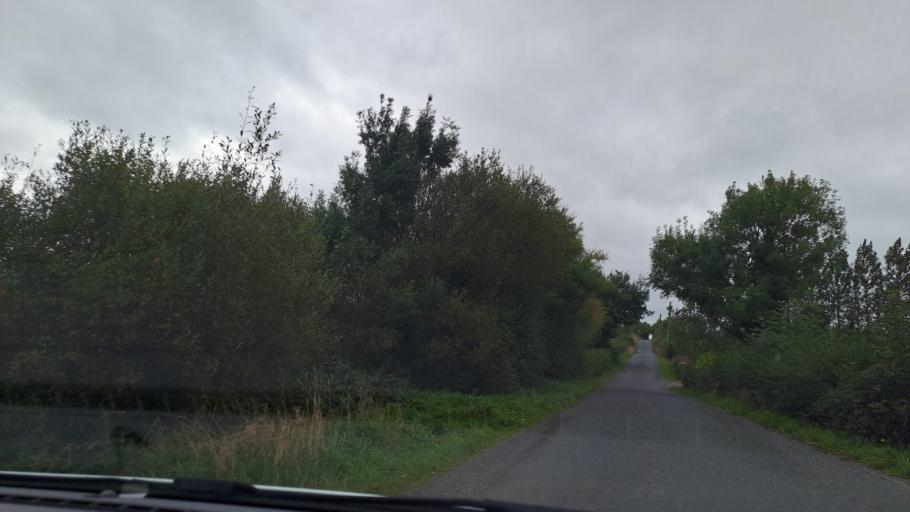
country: IE
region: Ulster
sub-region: An Cabhan
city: Kingscourt
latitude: 54.0150
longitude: -6.8788
